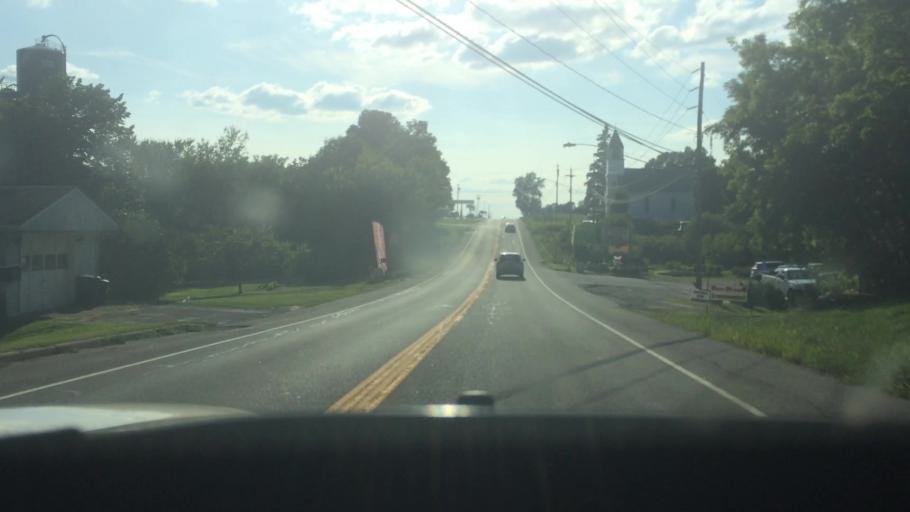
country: US
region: New York
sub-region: St. Lawrence County
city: Potsdam
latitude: 44.6899
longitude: -74.7052
